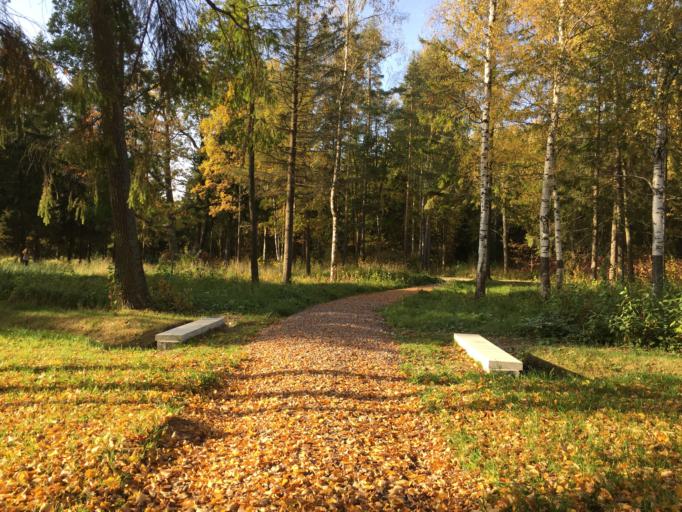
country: RU
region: St.-Petersburg
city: Pushkin
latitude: 59.7158
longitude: 30.3794
